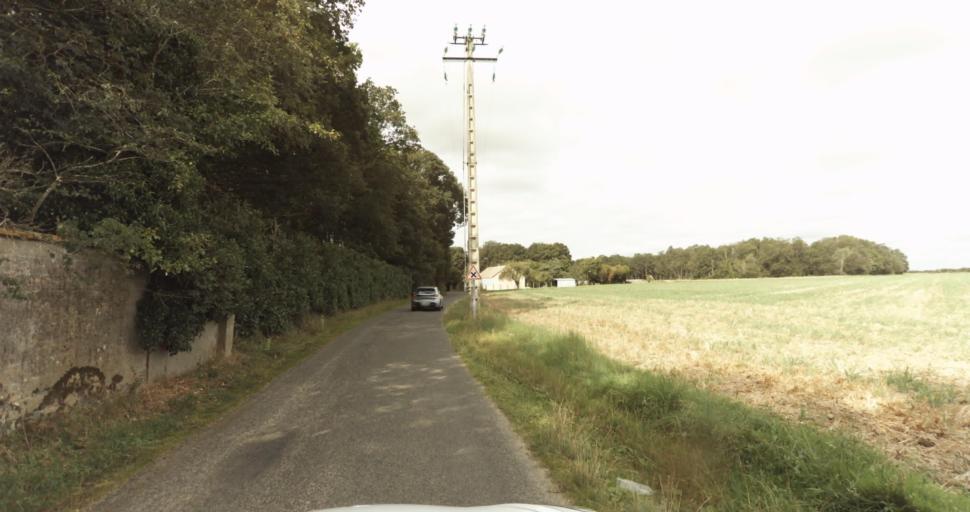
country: FR
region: Haute-Normandie
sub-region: Departement de l'Eure
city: Tillieres-sur-Avre
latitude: 48.7753
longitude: 1.0920
